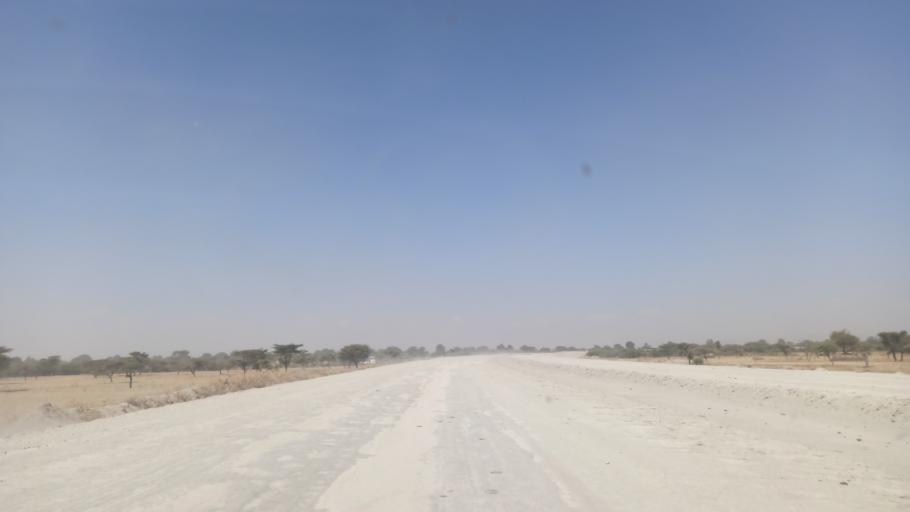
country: ET
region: Oromiya
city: Ziway
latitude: 7.6952
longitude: 38.6474
